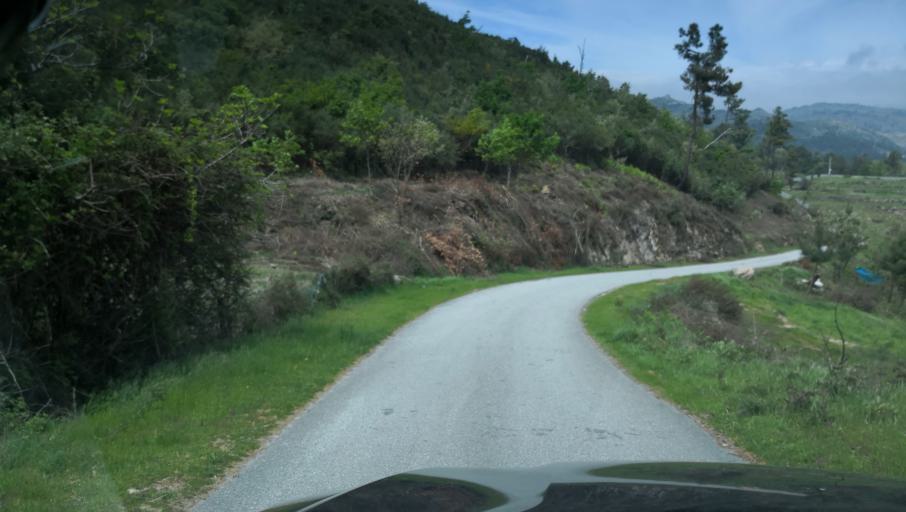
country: PT
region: Vila Real
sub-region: Vila Real
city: Vila Real
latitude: 41.3009
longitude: -7.8034
